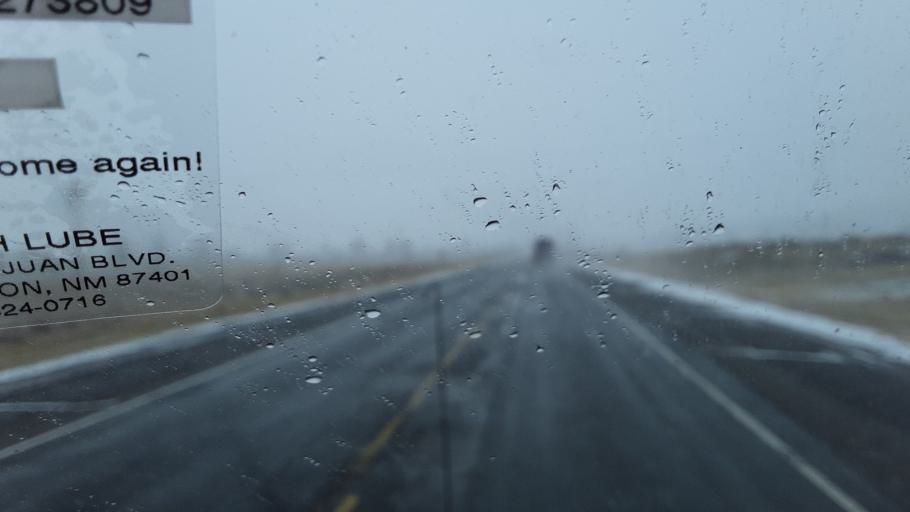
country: US
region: New Mexico
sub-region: Rio Arriba County
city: Chama
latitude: 36.8479
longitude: -106.5724
